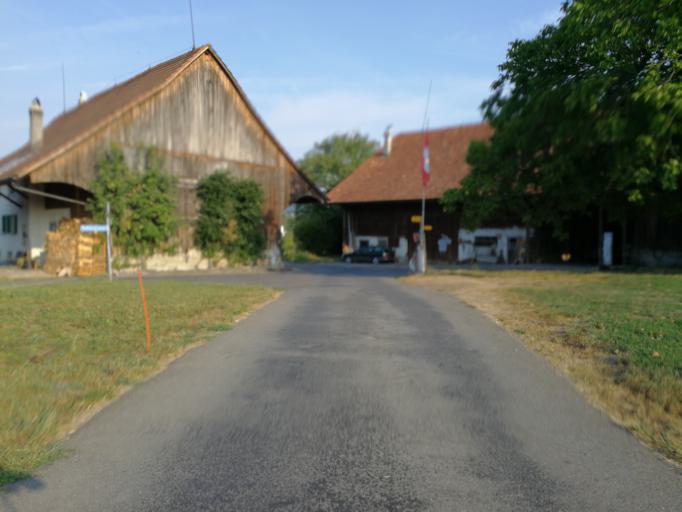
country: CH
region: Zurich
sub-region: Bezirk Uster
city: Esslingen
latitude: 47.2888
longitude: 8.7168
